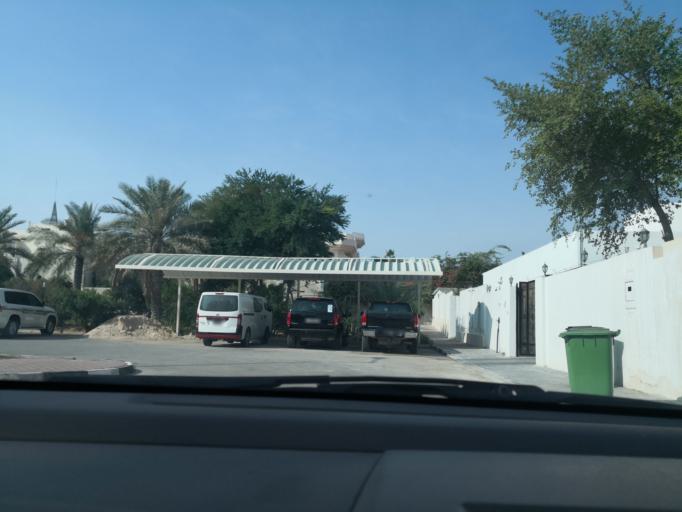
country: QA
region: Baladiyat ad Dawhah
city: Doha
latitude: 25.3311
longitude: 51.5084
